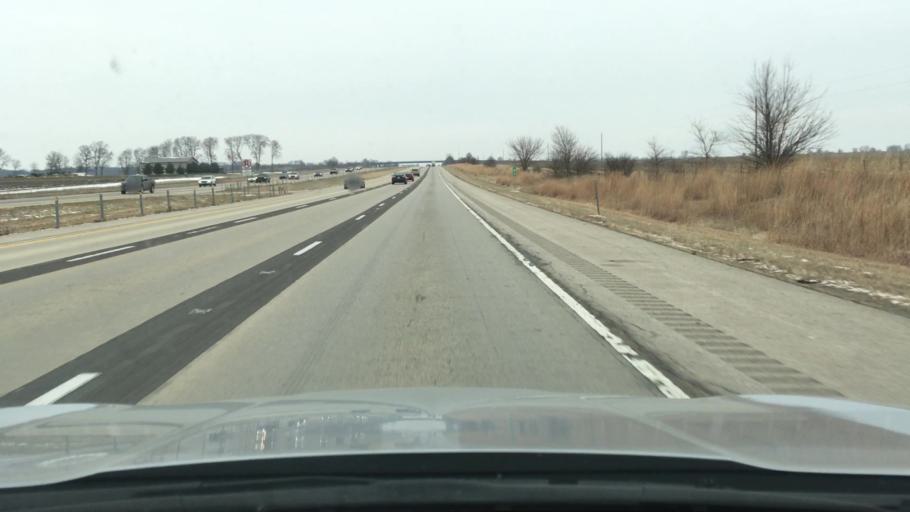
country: US
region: Illinois
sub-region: Sangamon County
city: Chatham
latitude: 39.6380
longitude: -89.6470
